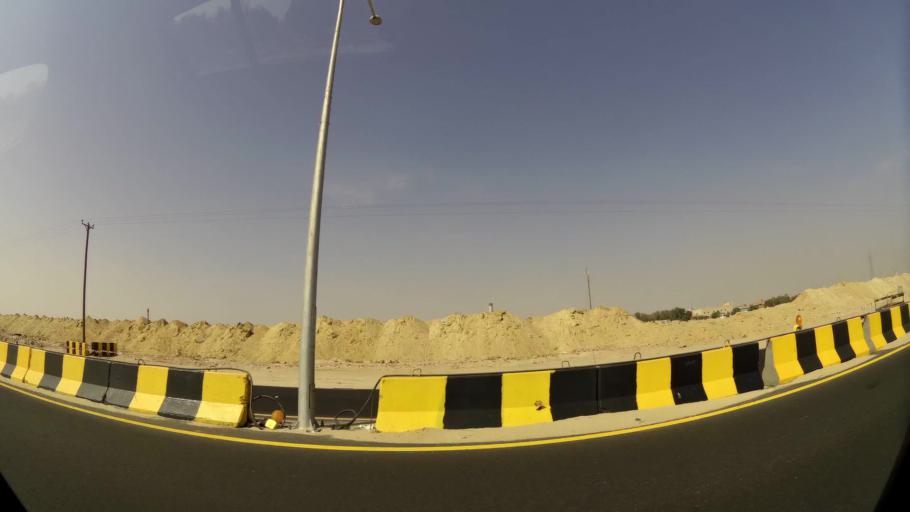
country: KW
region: Al Ahmadi
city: Al Fahahil
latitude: 28.9900
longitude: 48.1391
